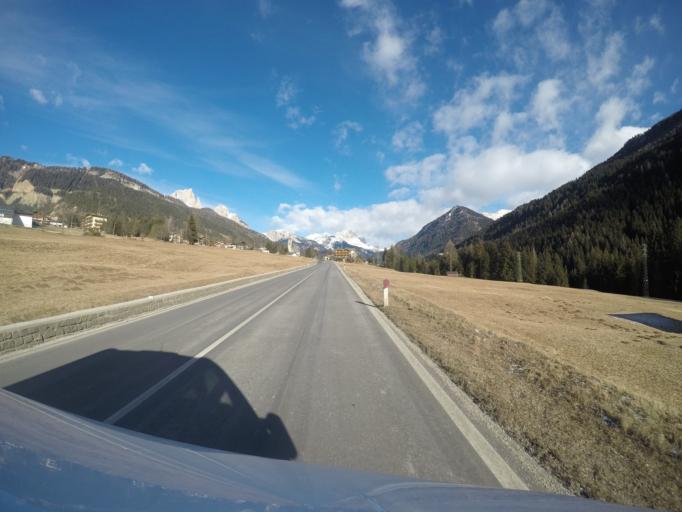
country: IT
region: Trentino-Alto Adige
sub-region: Provincia di Trento
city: Vigo di Fassa
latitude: 46.4156
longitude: 11.6793
